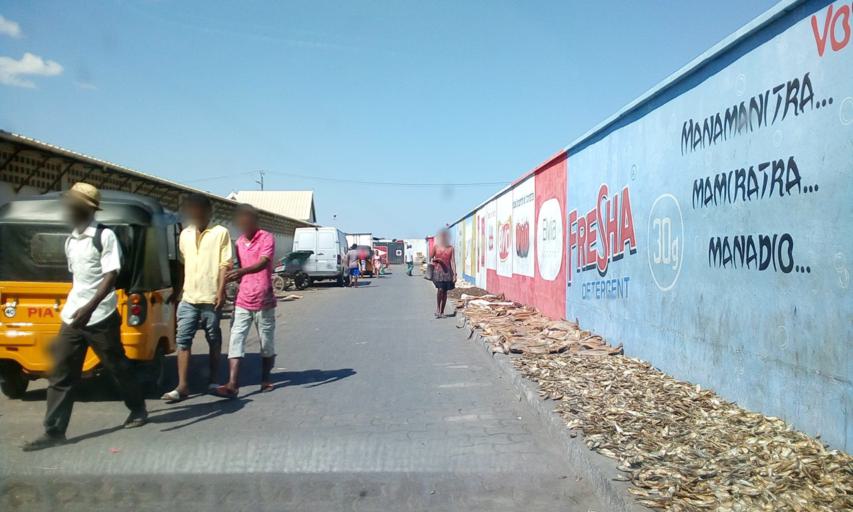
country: MG
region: Boeny
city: Mahajanga
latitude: -15.7249
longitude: 46.3179
